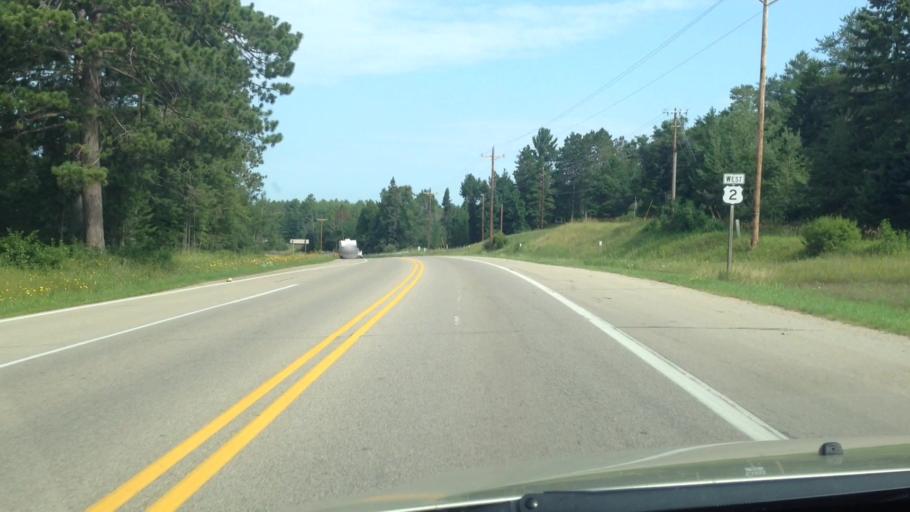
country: US
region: Michigan
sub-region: Delta County
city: Gladstone
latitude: 45.9209
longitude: -86.9351
